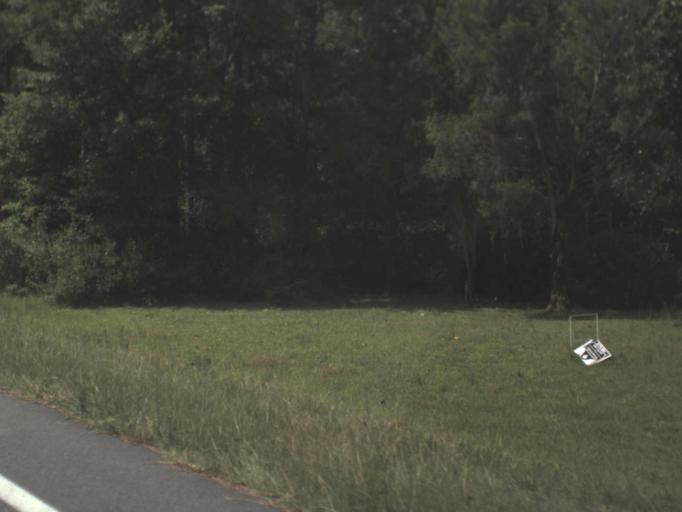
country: US
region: Florida
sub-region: Hamilton County
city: Jasper
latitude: 30.5306
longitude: -82.9690
